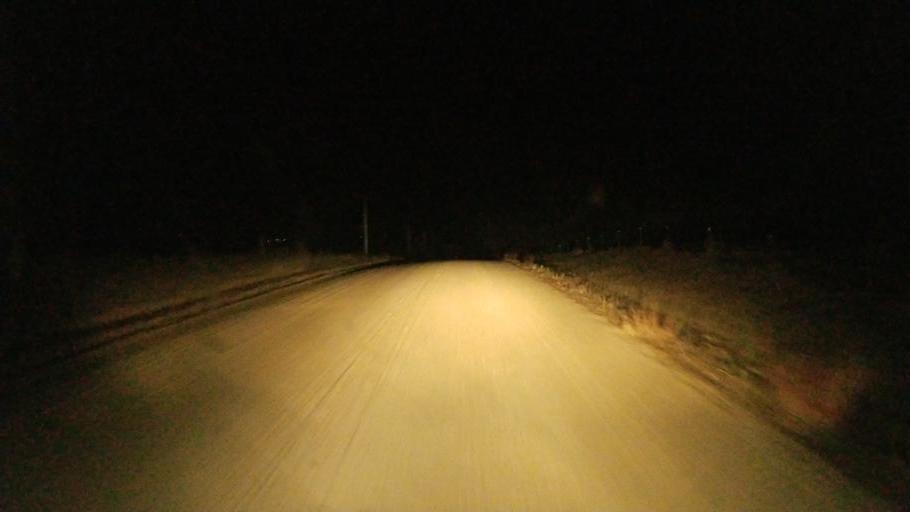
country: US
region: Nebraska
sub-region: Knox County
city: Center
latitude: 42.6260
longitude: -97.8259
